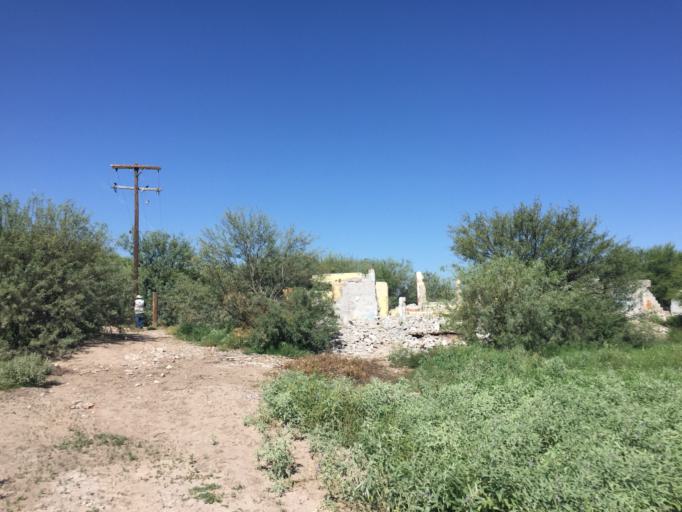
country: MX
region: Durango
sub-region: Gomez Palacio
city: San Felipe
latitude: 25.7277
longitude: -103.3759
